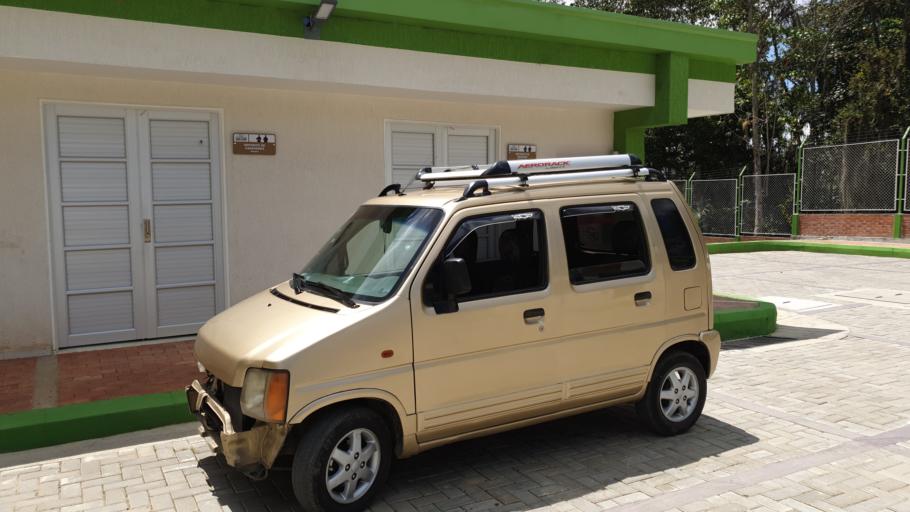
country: CO
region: Boyaca
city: Santana
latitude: 6.0524
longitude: -73.4873
